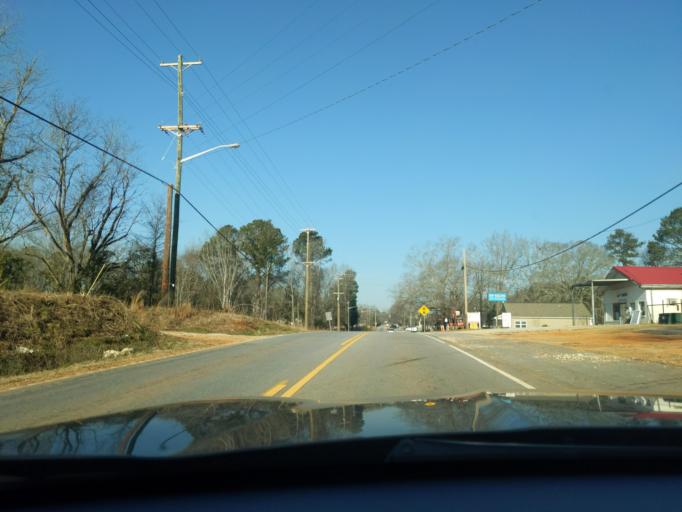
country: US
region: South Carolina
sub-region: Greenwood County
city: Greenwood
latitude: 34.1941
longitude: -82.1281
